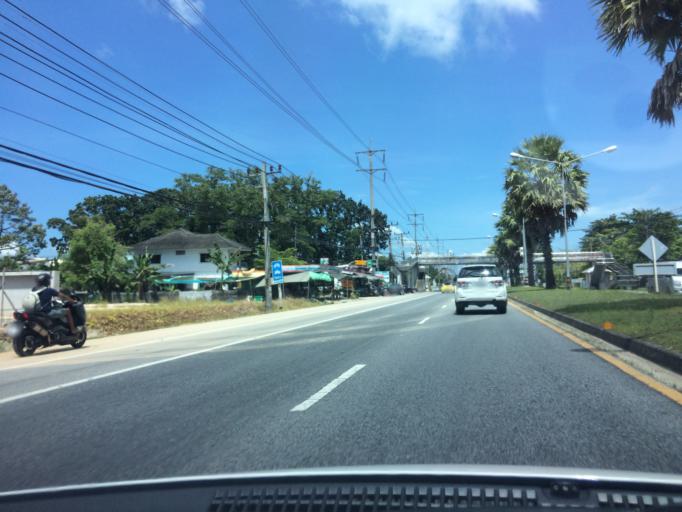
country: TH
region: Phuket
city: Thalang
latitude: 8.0652
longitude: 98.3419
